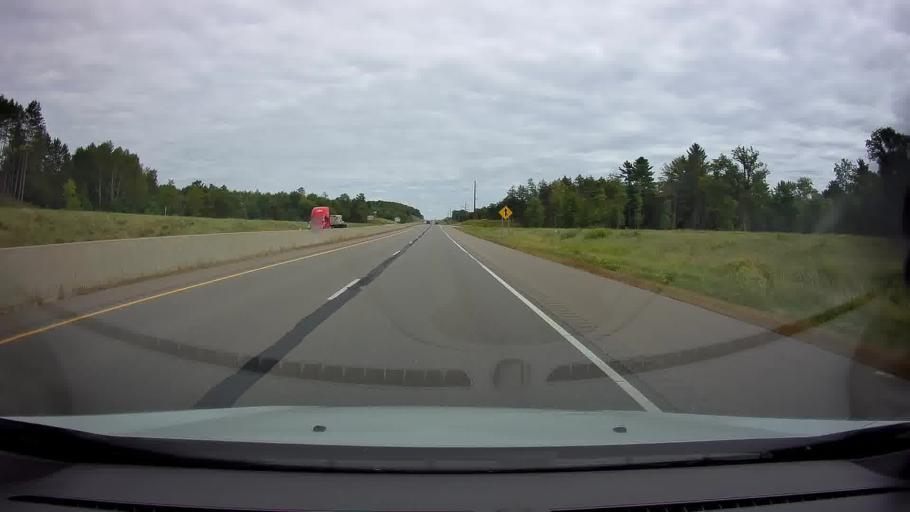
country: US
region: Wisconsin
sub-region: Marathon County
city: Marathon
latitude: 44.9440
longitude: -89.7843
